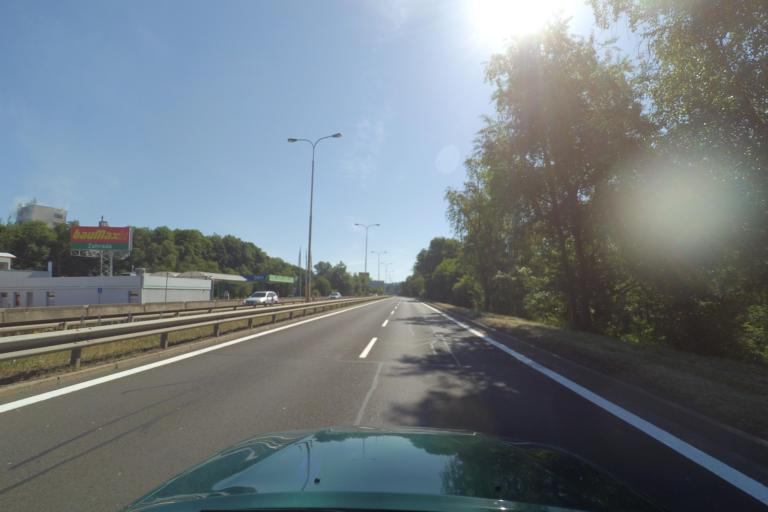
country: CZ
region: Karlovarsky
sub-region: Okres Karlovy Vary
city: Karlovy Vary
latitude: 50.2309
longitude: 12.8537
